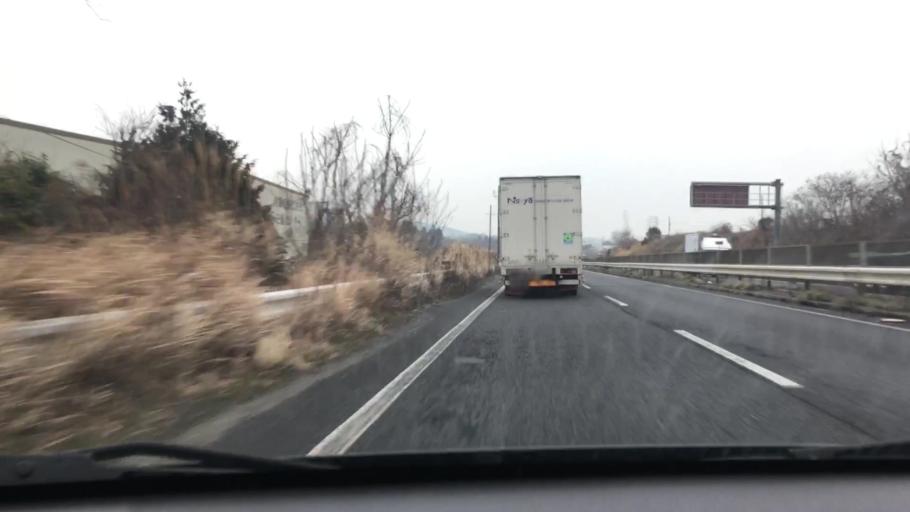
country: JP
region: Mie
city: Ueno-ebisumachi
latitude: 34.7126
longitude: 136.0789
